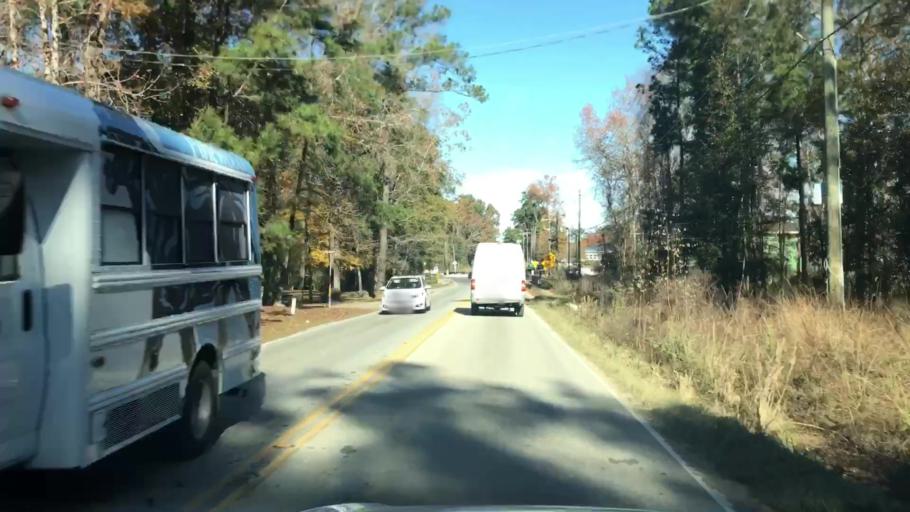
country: US
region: South Carolina
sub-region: Dorchester County
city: Summerville
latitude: 33.0210
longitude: -80.2412
